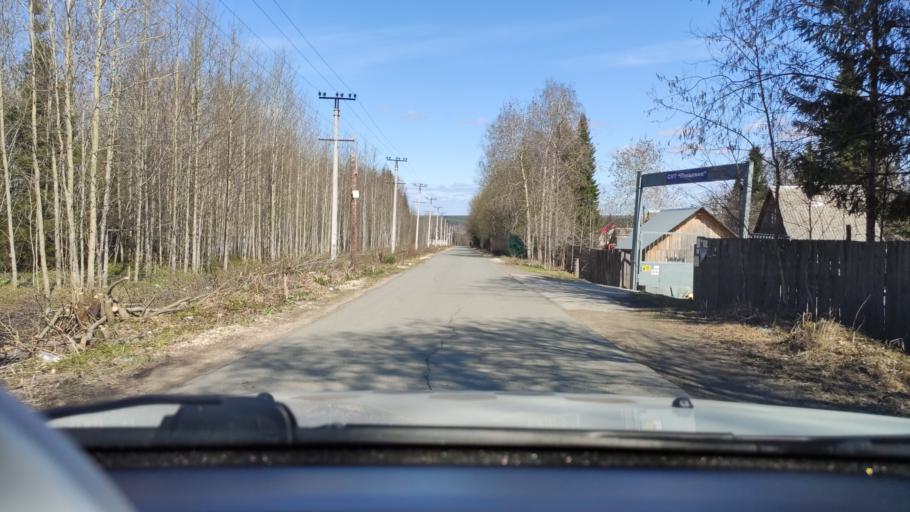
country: RU
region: Perm
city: Novyye Lyady
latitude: 58.0467
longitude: 56.6398
